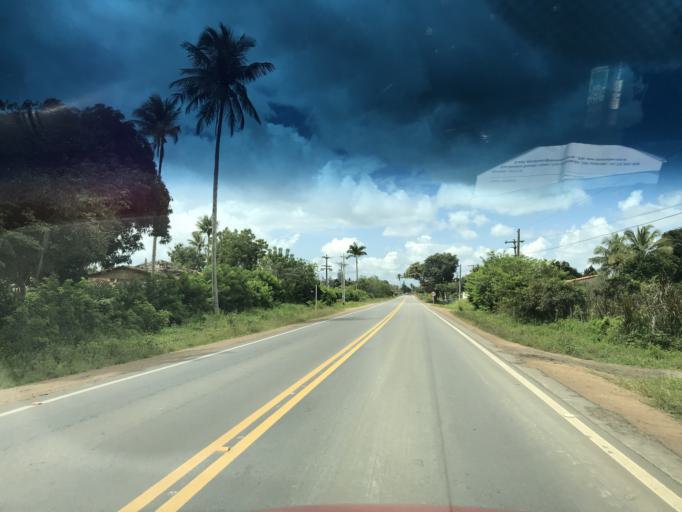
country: BR
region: Bahia
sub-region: Conceicao Do Almeida
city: Conceicao do Almeida
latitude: -12.7289
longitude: -39.1997
